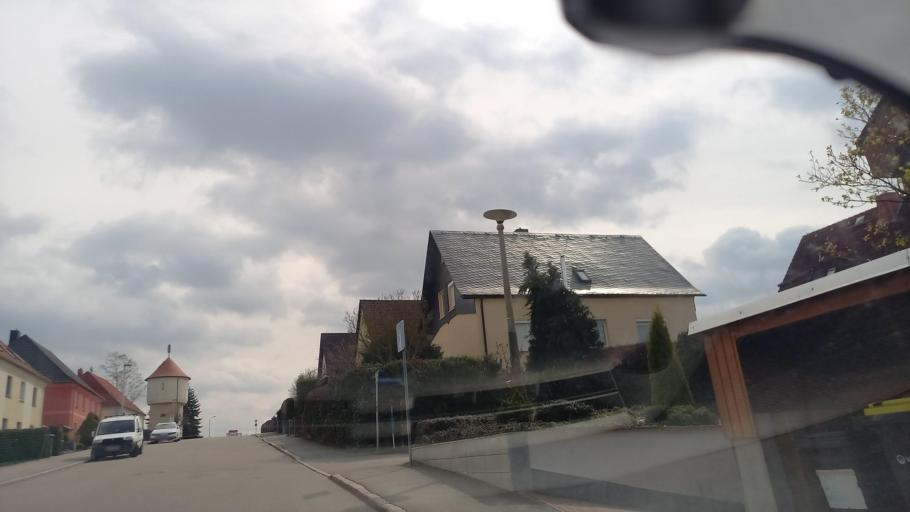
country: DE
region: Saxony
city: Wilkau-Hasslau
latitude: 50.6980
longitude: 12.5190
